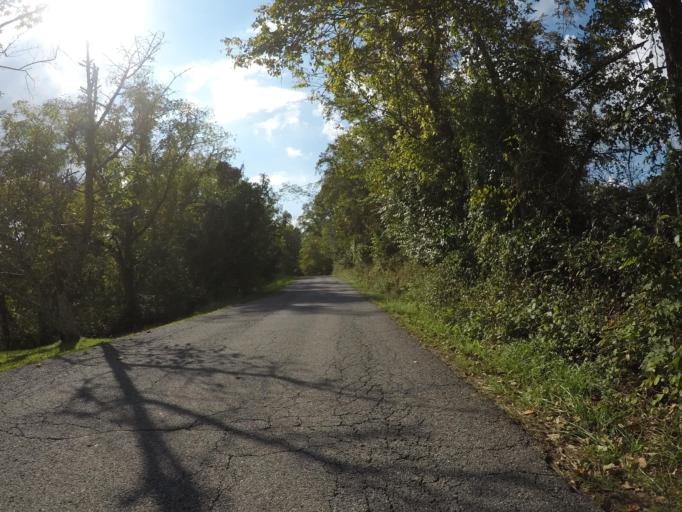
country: US
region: West Virginia
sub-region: Wayne County
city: Lavalette
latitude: 38.3640
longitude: -82.4621
